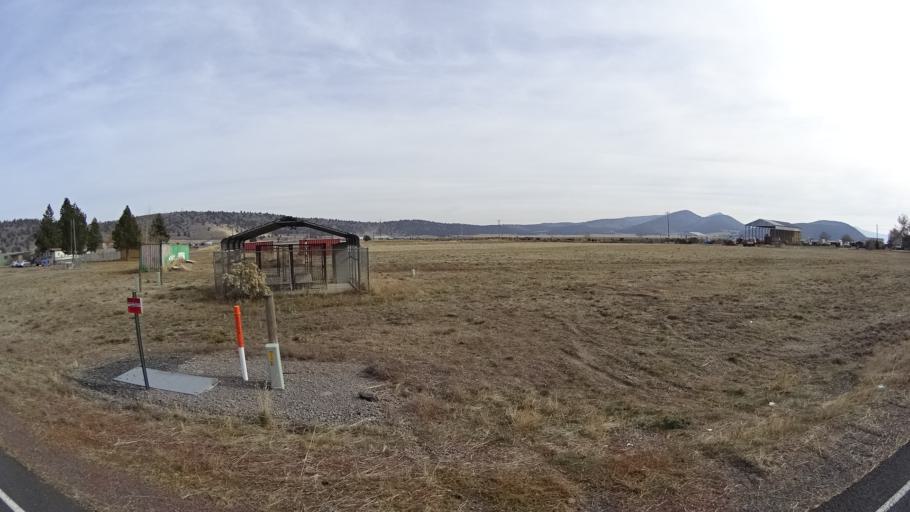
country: US
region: Oregon
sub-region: Klamath County
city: Klamath Falls
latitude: 41.9612
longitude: -121.9180
